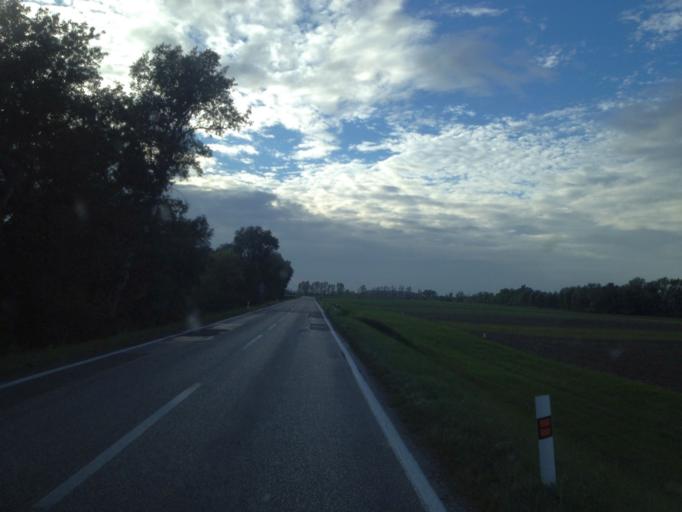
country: HU
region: Komarom-Esztergom
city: Almasfuzito
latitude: 47.7409
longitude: 18.2790
